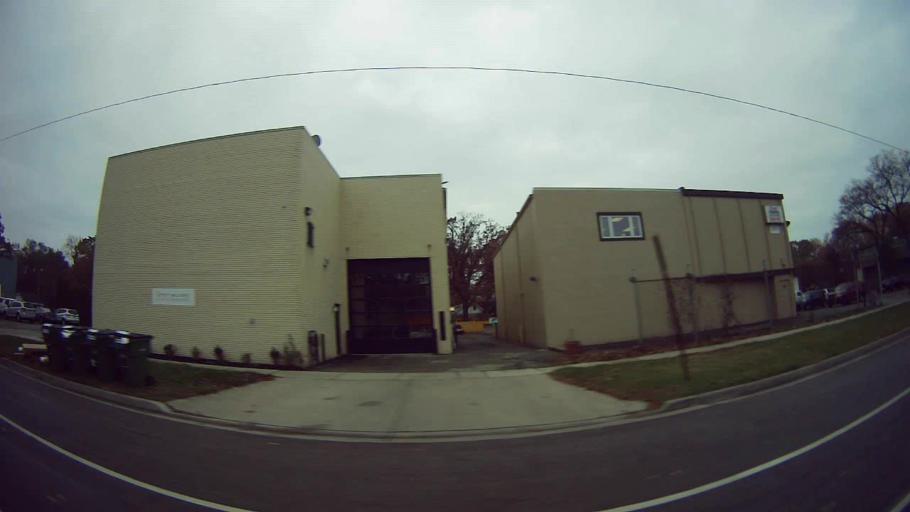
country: US
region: Michigan
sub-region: Oakland County
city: Ferndale
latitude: 42.4484
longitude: -83.1423
